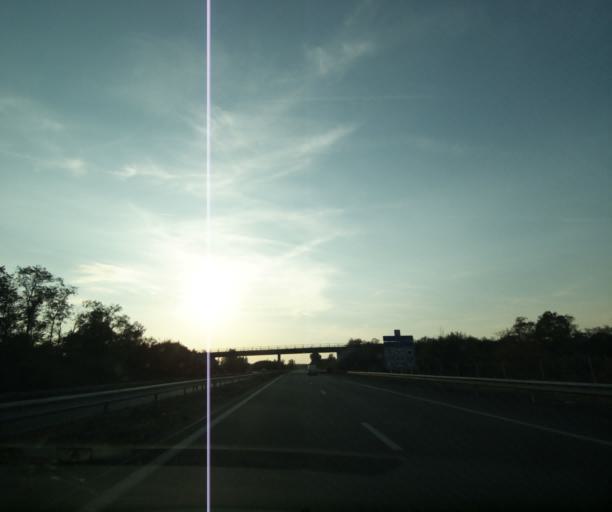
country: FR
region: Midi-Pyrenees
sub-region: Departement du Tarn-et-Garonne
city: Saint-Nicolas-de-la-Grave
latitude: 44.0415
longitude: 1.0131
